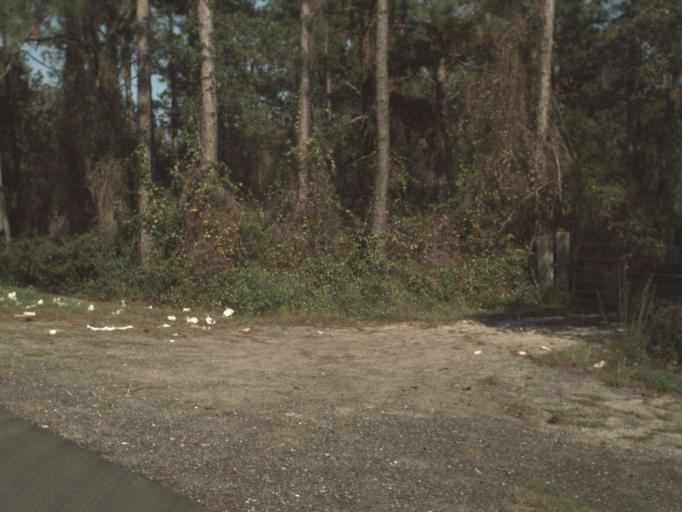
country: US
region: Florida
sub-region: Gulf County
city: Port Saint Joe
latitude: 29.8280
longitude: -85.2789
